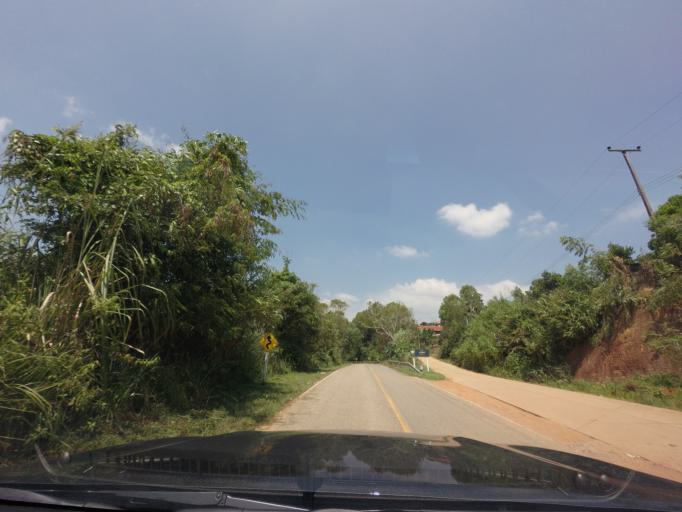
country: TH
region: Loei
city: Na Haeo
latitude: 17.5964
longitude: 100.9035
